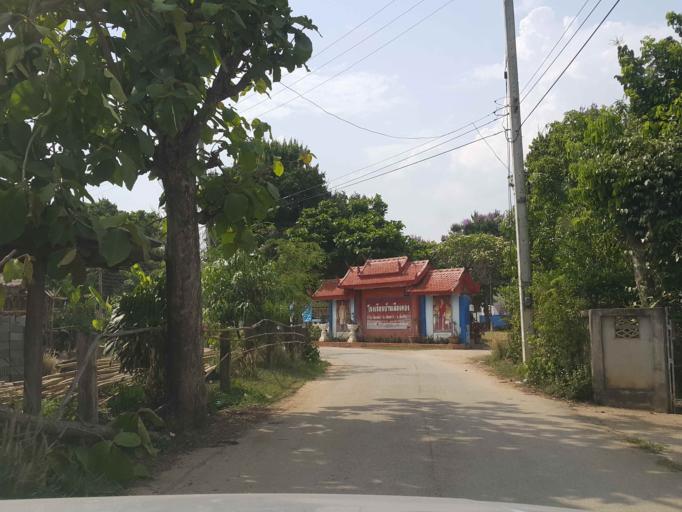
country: TH
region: Chiang Mai
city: Wiang Haeng
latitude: 19.3838
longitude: 98.7173
